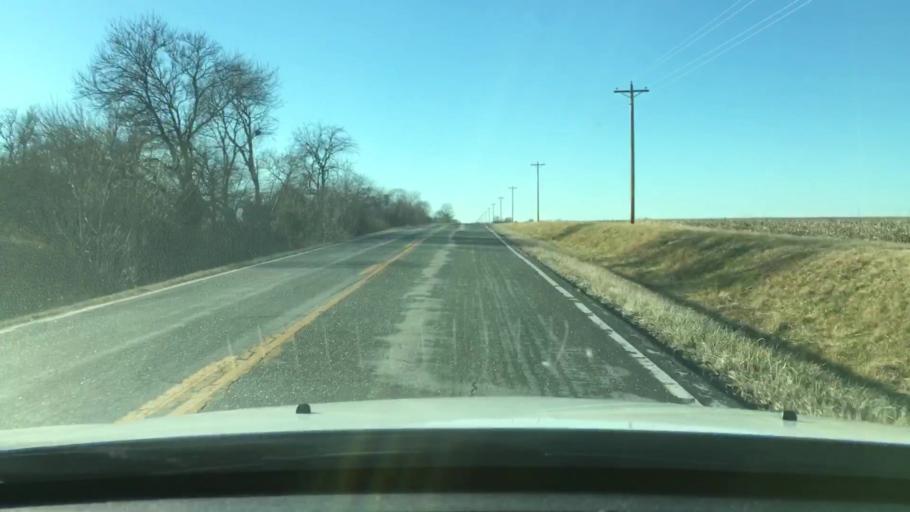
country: US
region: Missouri
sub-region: Audrain County
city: Mexico
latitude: 39.2816
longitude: -91.7228
